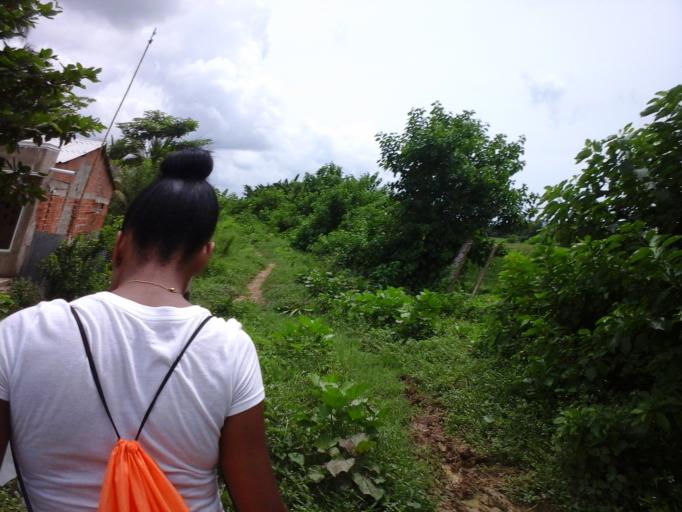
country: CO
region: Bolivar
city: San Pablo
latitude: 10.1467
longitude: -75.2764
